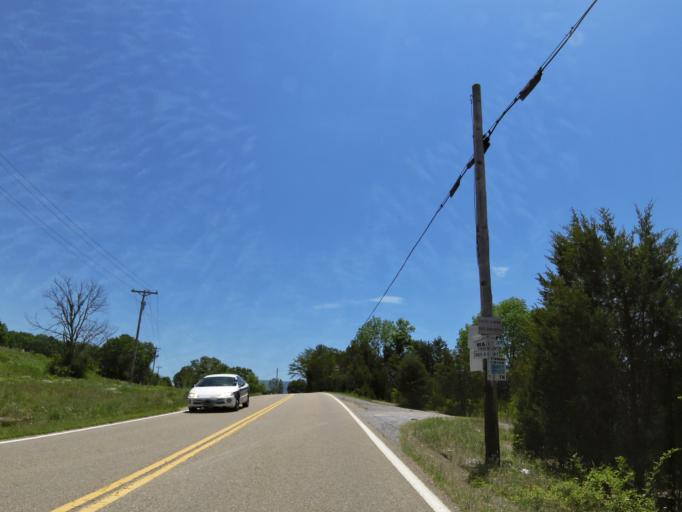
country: US
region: Tennessee
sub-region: Jefferson County
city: Dandridge
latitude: 35.9642
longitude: -83.3900
